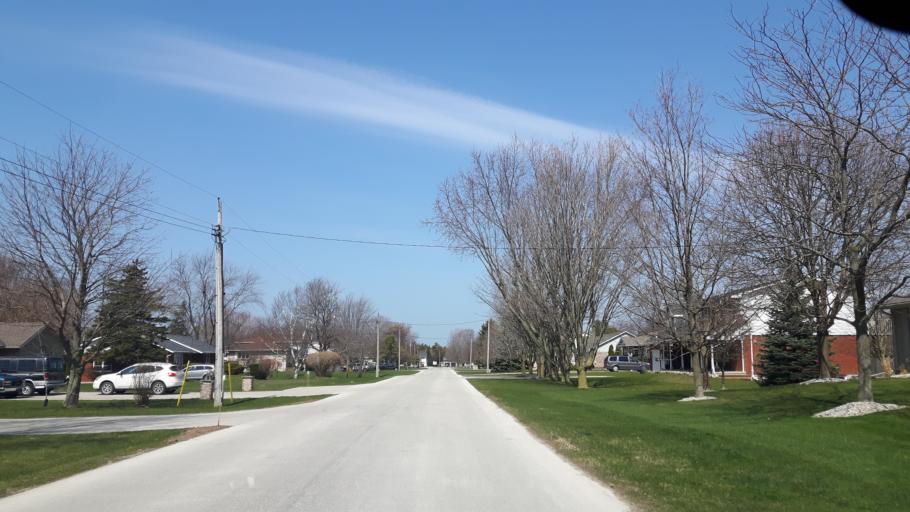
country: CA
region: Ontario
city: Goderich
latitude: 43.7243
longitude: -81.6834
